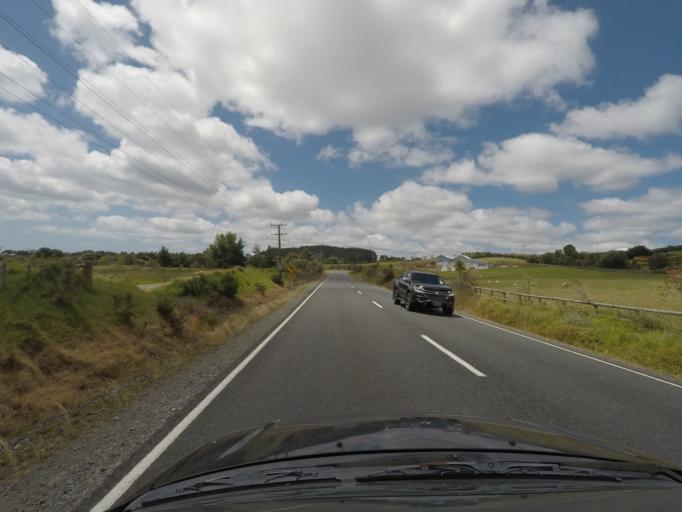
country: NZ
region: Northland
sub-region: Whangarei
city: Ruakaka
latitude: -36.0123
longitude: 174.4827
